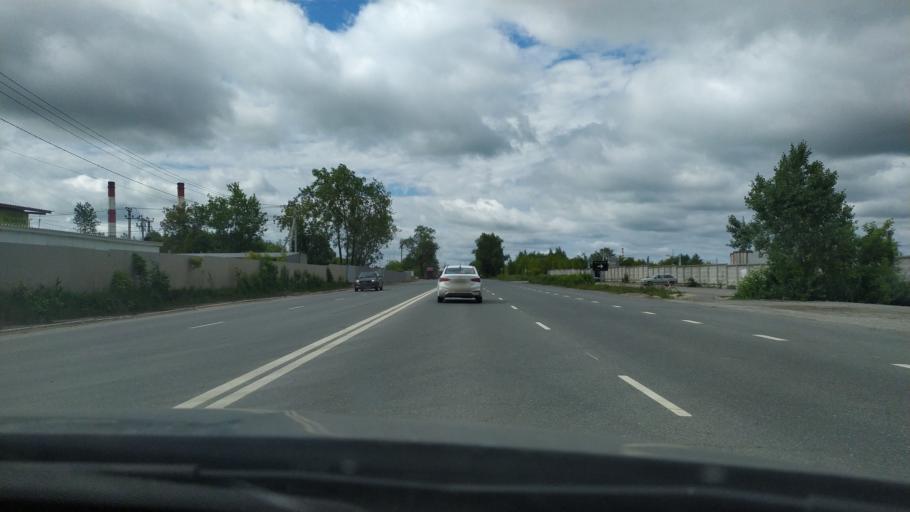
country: RU
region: Perm
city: Kondratovo
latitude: 57.9330
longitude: 56.1516
